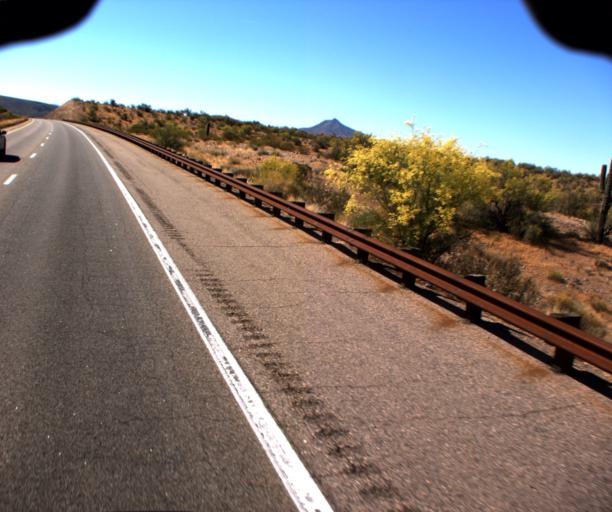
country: US
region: Arizona
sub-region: Yavapai County
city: Bagdad
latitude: 34.5959
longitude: -113.5166
